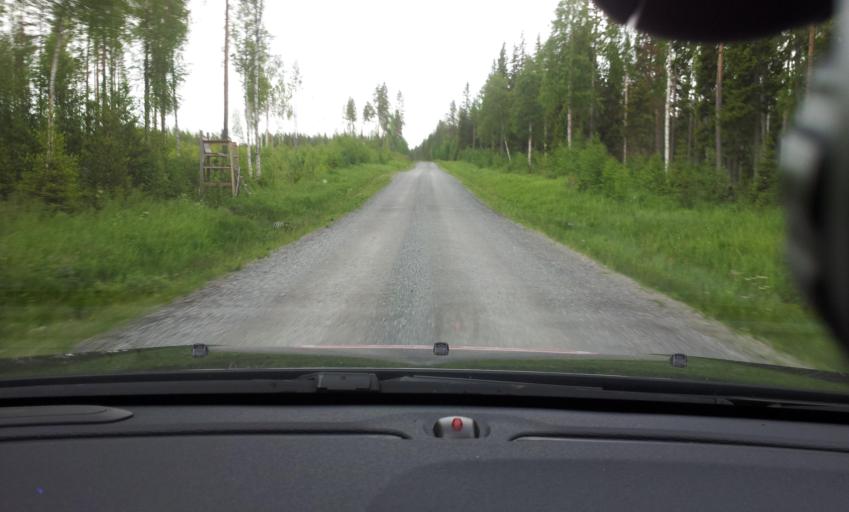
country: SE
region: Jaemtland
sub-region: OEstersunds Kommun
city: Brunflo
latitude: 63.1392
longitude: 15.0649
